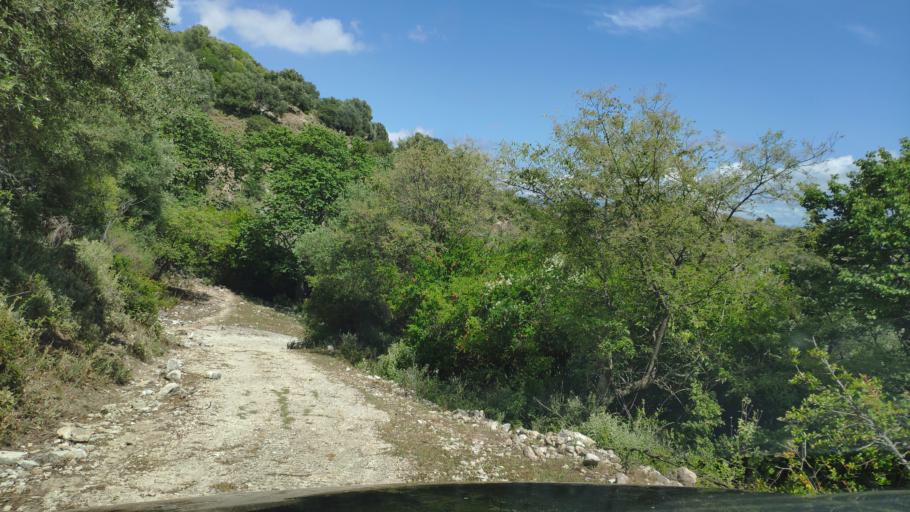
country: AL
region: Vlore
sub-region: Rrethi i Sarandes
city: Konispol
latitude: 39.6380
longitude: 20.2043
